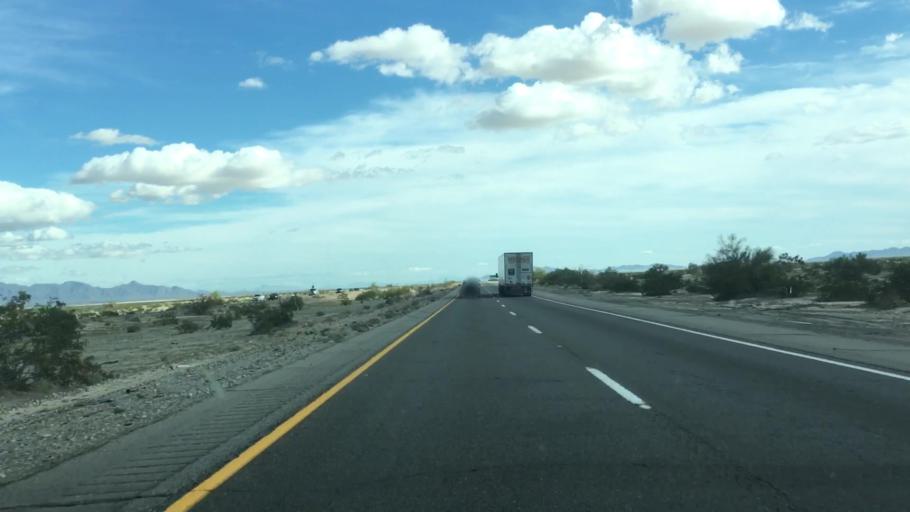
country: US
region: California
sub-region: Riverside County
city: Mesa Verde
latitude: 33.6464
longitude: -115.1220
